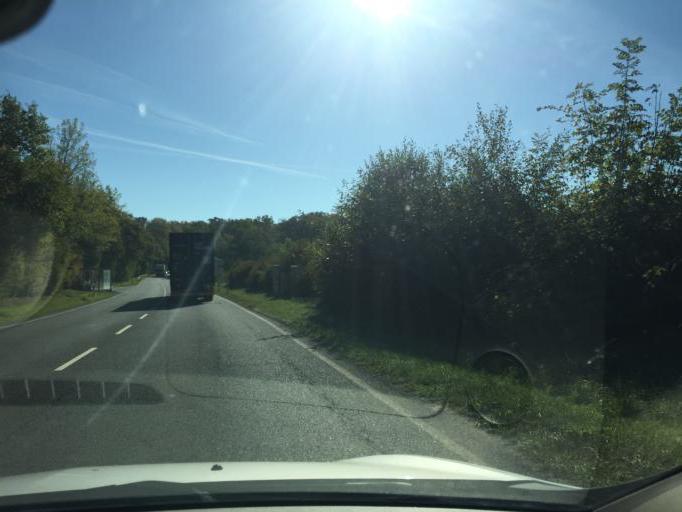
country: LU
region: Luxembourg
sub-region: Canton de Luxembourg
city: Sandweiler
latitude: 49.6073
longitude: 6.2026
